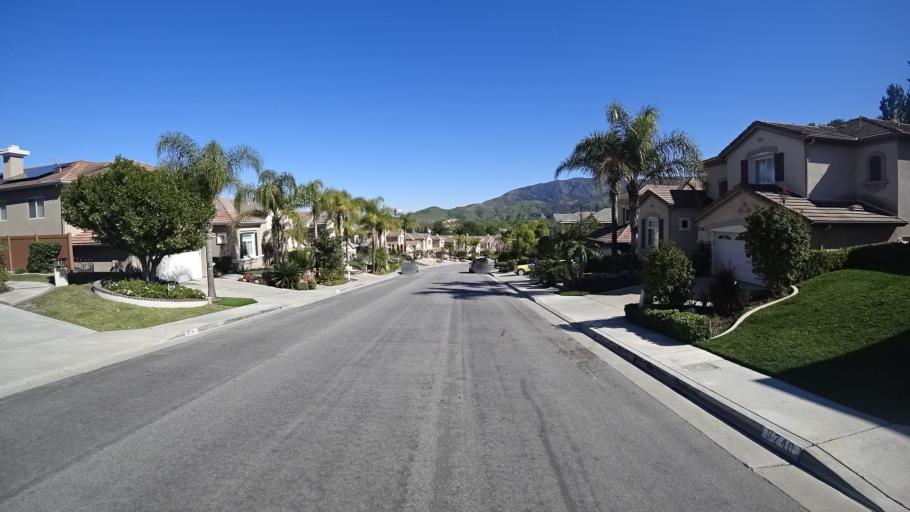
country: US
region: California
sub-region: Orange County
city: Yorba Linda
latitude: 33.8598
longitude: -117.7235
